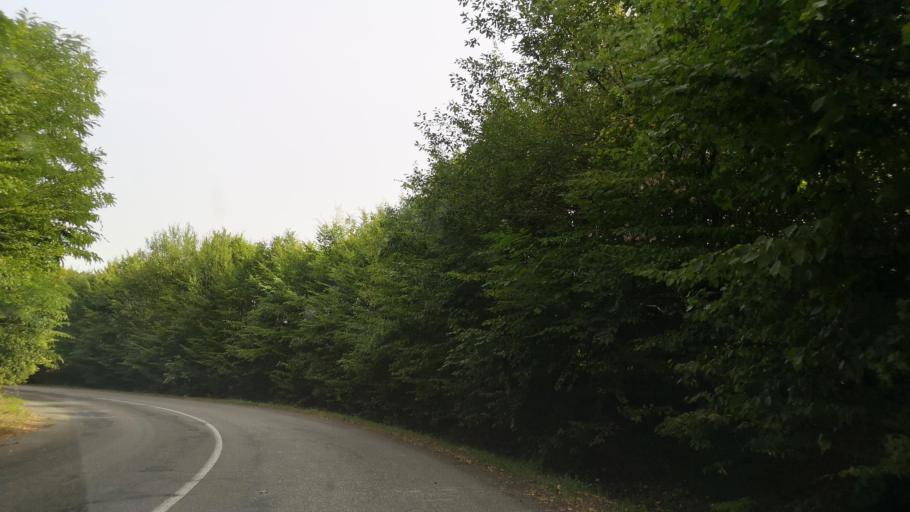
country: SK
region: Banskobystricky
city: Revuca
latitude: 48.5818
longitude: 20.0716
